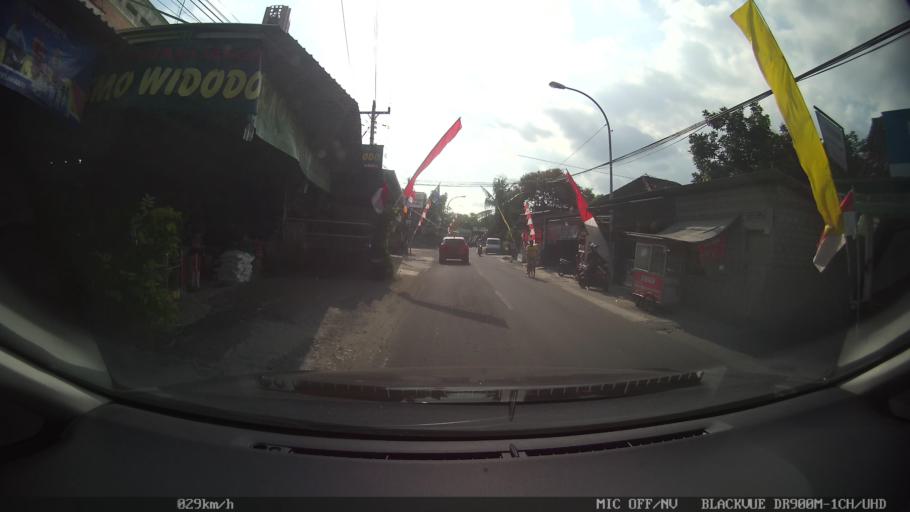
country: ID
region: Daerah Istimewa Yogyakarta
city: Kasihan
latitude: -7.8286
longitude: 110.3316
